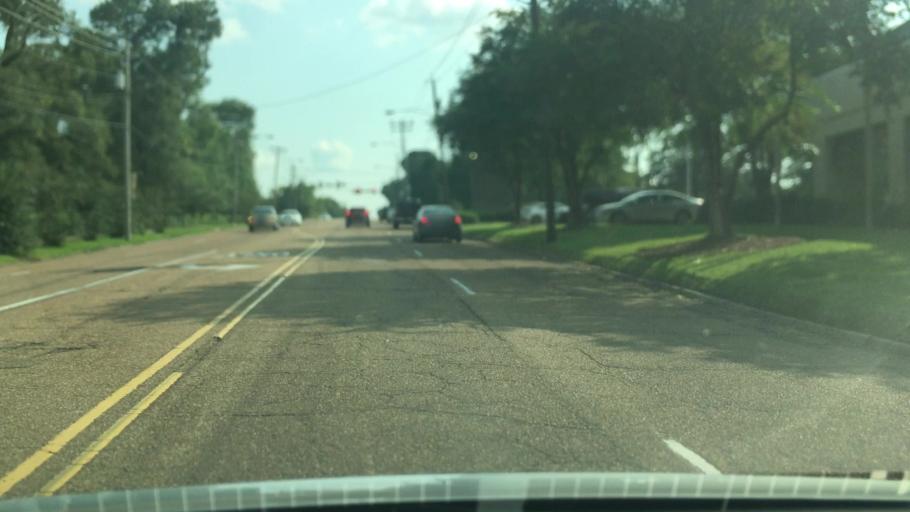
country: US
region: Mississippi
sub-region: Hinds County
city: Jackson
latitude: 32.3253
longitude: -90.1762
